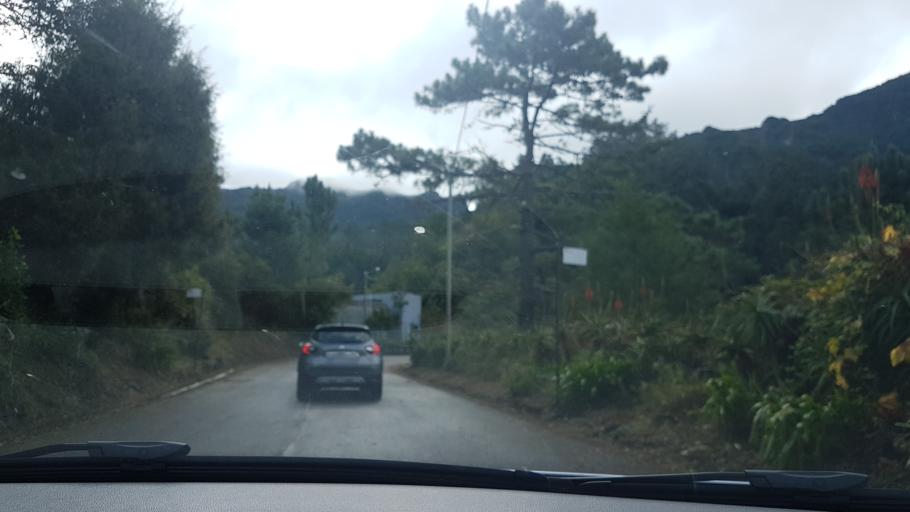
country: PT
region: Madeira
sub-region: Sao Vicente
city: Sao Vicente
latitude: 32.7730
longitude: -17.0269
